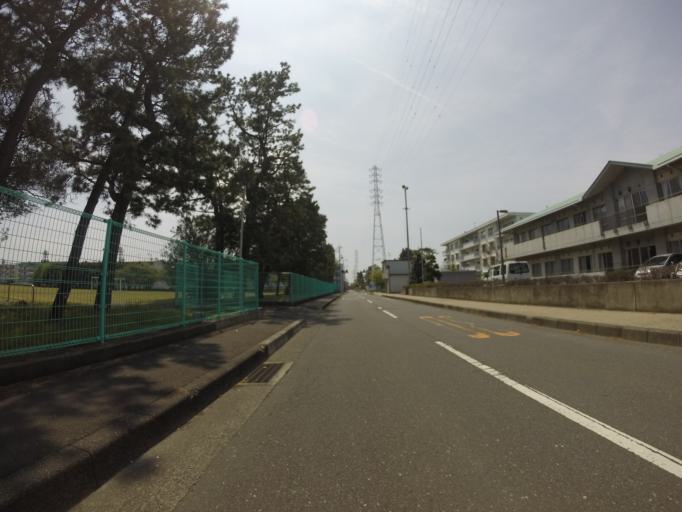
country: JP
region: Shizuoka
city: Shizuoka-shi
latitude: 34.9868
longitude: 138.5120
